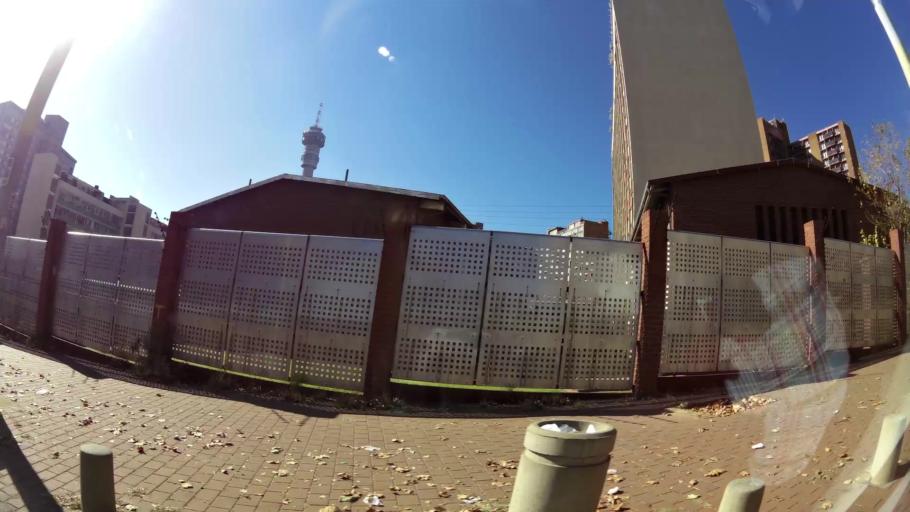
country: ZA
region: Gauteng
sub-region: City of Johannesburg Metropolitan Municipality
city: Johannesburg
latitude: -26.1879
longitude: 28.0442
